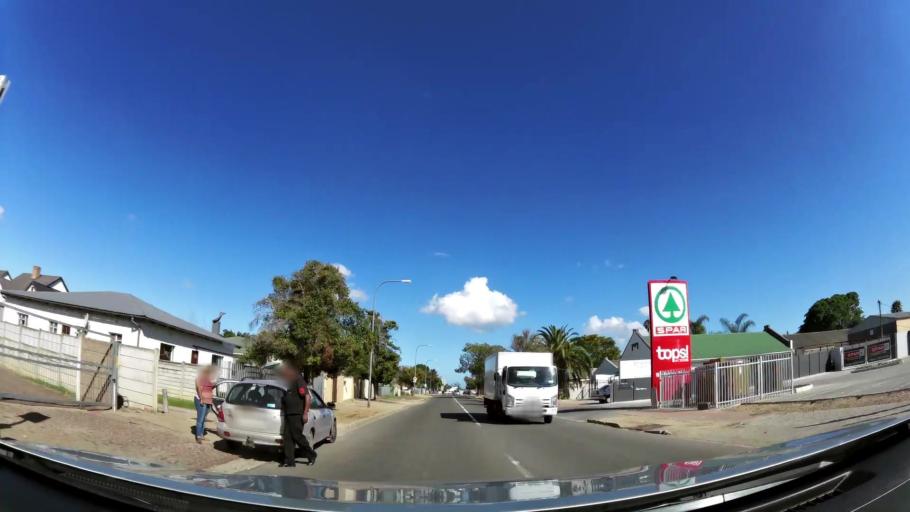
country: ZA
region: Western Cape
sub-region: Eden District Municipality
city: George
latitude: -33.9544
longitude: 22.4679
